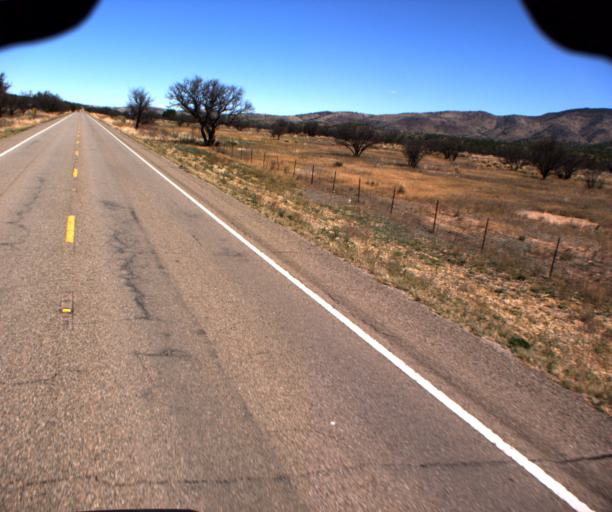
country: US
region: Arizona
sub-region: Santa Cruz County
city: Rio Rico
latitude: 31.5764
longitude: -110.7291
